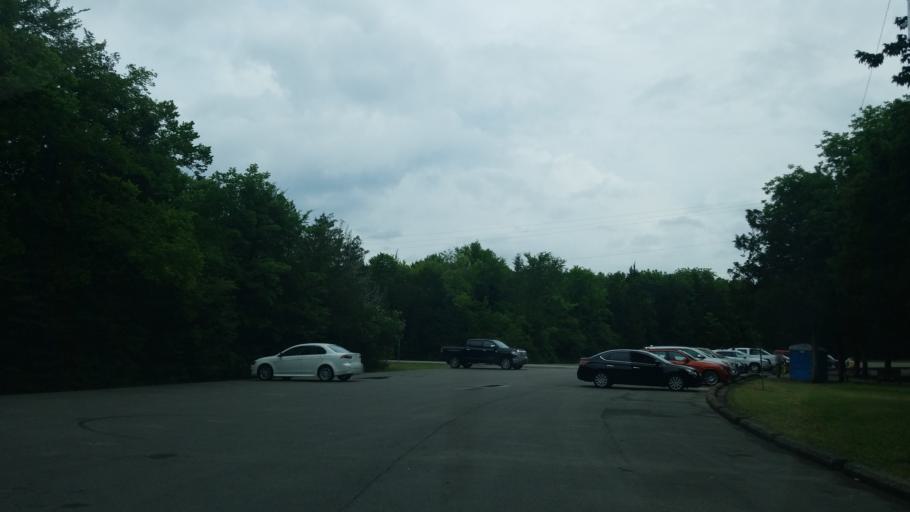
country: US
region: Tennessee
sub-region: Rutherford County
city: La Vergne
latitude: 36.1042
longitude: -86.6244
